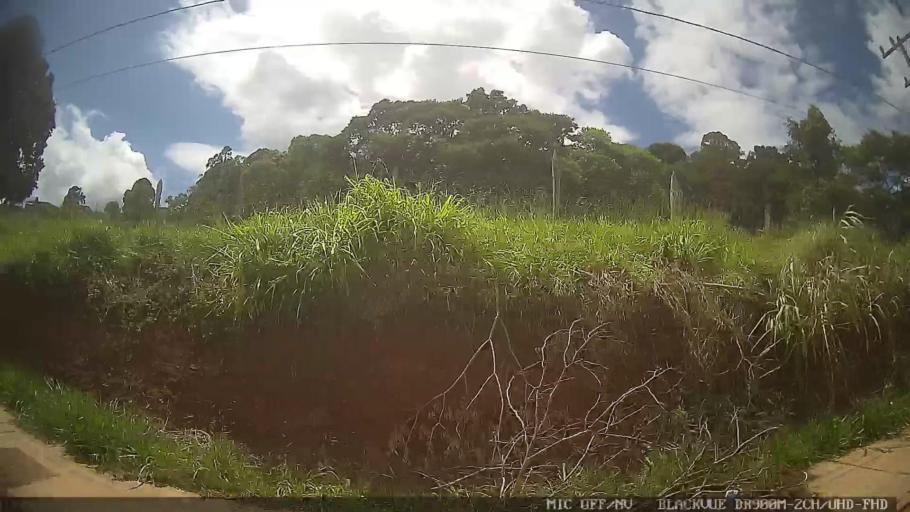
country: BR
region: Minas Gerais
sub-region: Extrema
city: Extrema
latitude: -22.7937
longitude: -46.4460
